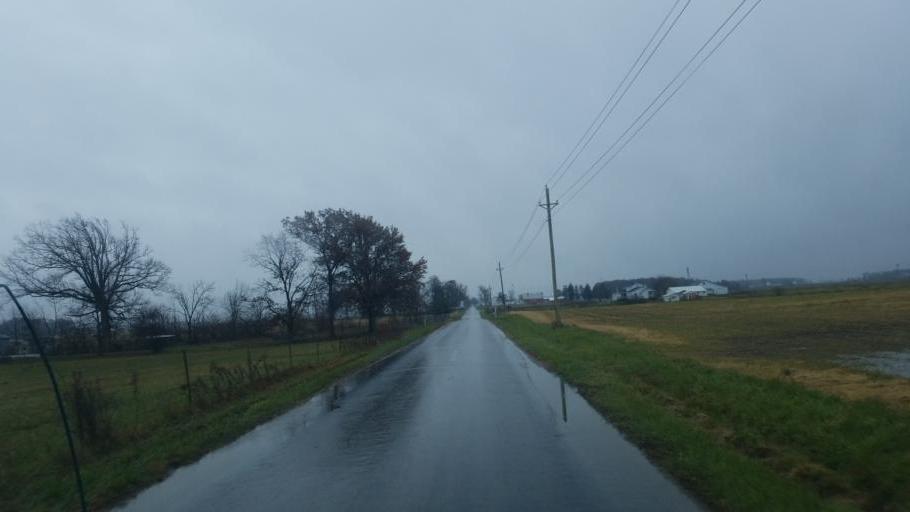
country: US
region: Indiana
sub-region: Adams County
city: Berne
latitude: 40.6471
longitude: -84.8784
